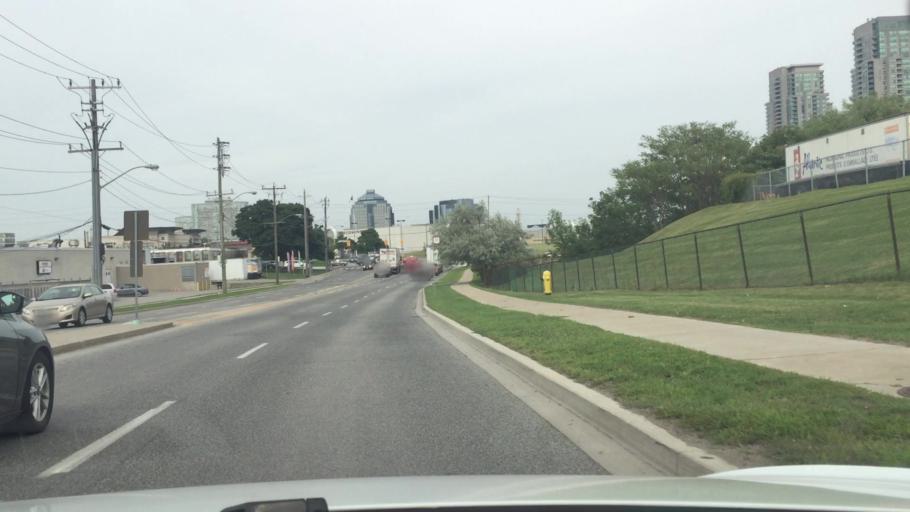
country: CA
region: Ontario
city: Scarborough
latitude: 43.7747
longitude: -79.2657
